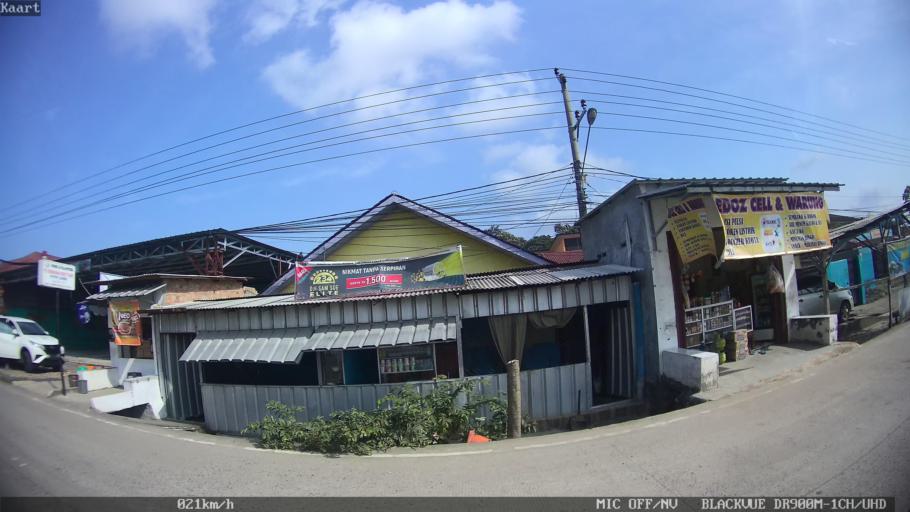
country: ID
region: Lampung
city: Kedaton
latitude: -5.3614
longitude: 105.2267
